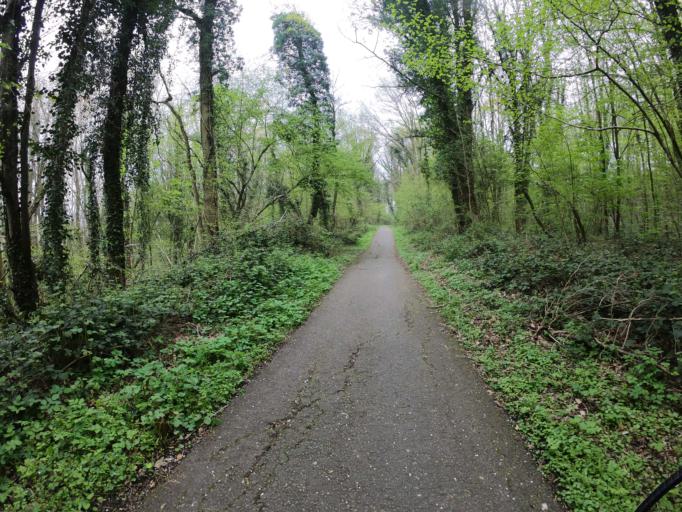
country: BE
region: Wallonia
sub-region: Province du Hainaut
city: Ellezelles
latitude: 50.7416
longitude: 3.6420
